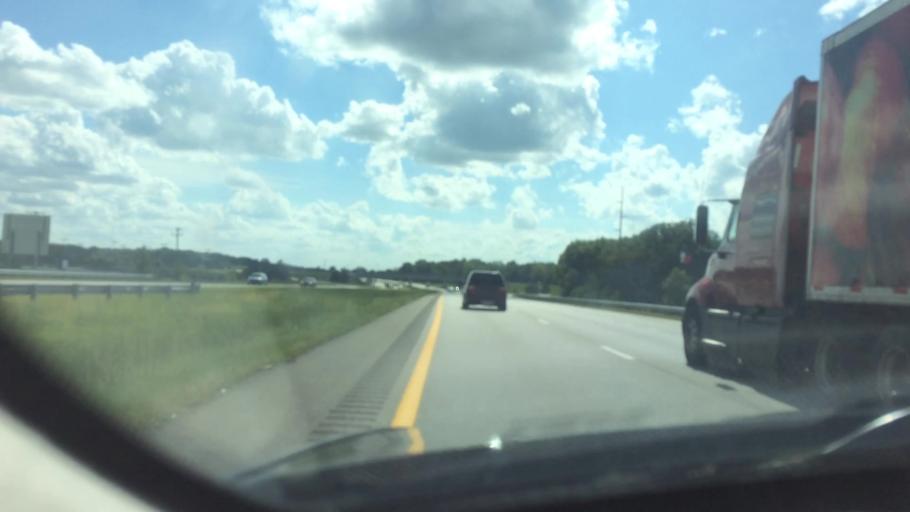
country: US
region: Ohio
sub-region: Shelby County
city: Sidney
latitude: 40.3173
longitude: -84.1707
